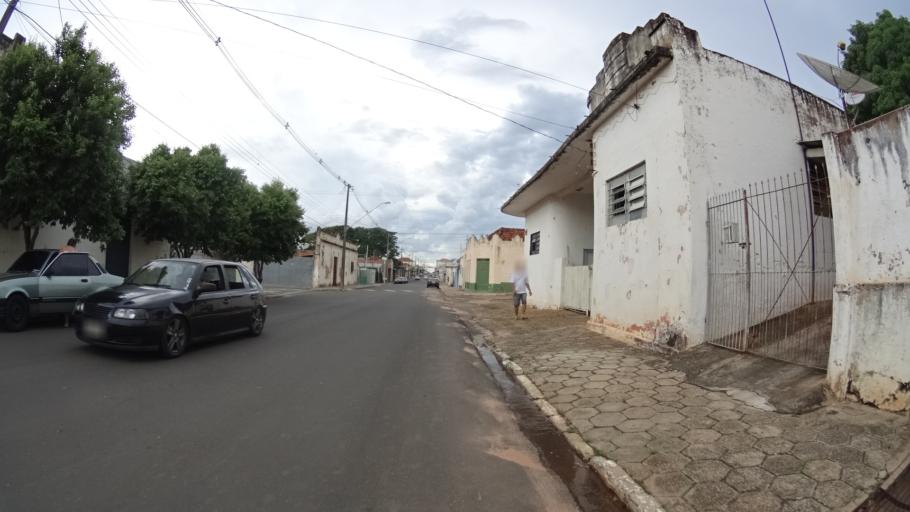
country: BR
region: Sao Paulo
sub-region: Marilia
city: Marilia
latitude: -22.2173
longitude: -49.8267
